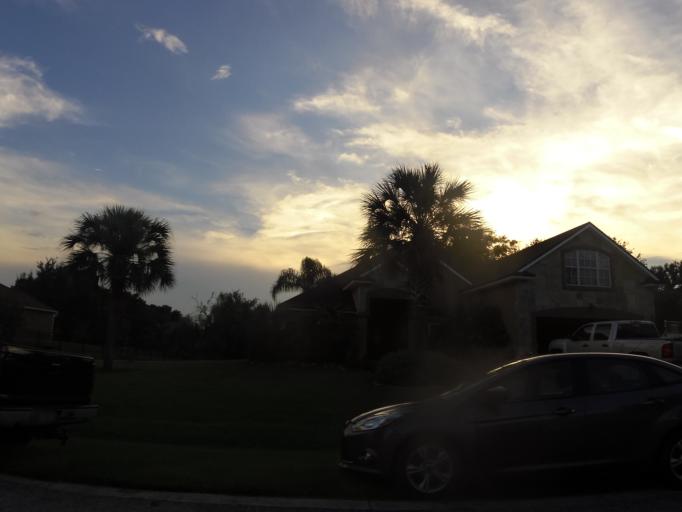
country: US
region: Florida
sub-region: Duval County
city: Atlantic Beach
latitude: 30.3967
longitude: -81.4963
